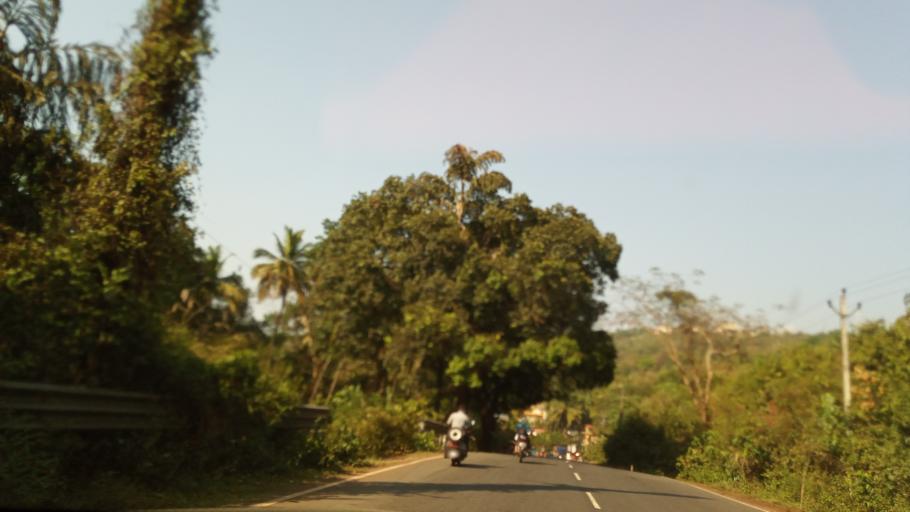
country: IN
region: Goa
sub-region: North Goa
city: Jua
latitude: 15.4717
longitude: 73.9633
